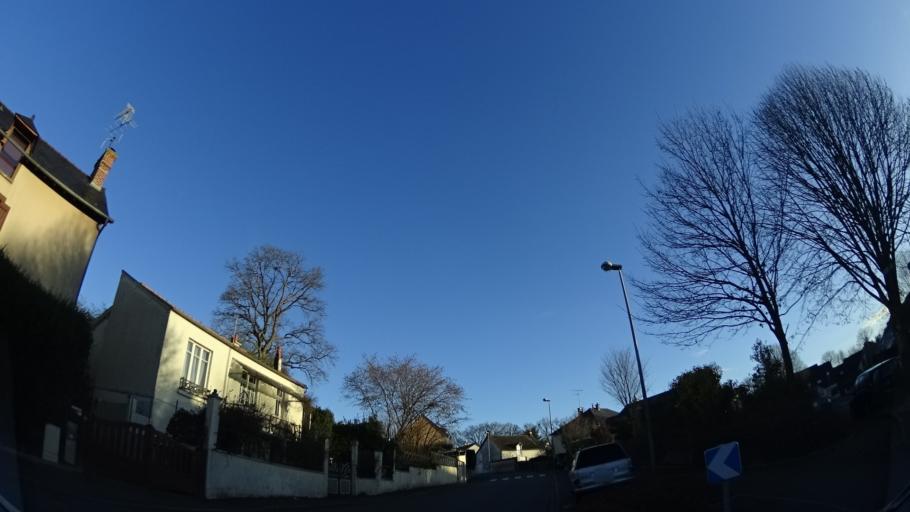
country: FR
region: Brittany
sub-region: Departement d'Ille-et-Vilaine
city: Betton
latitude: 48.1816
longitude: -1.6512
